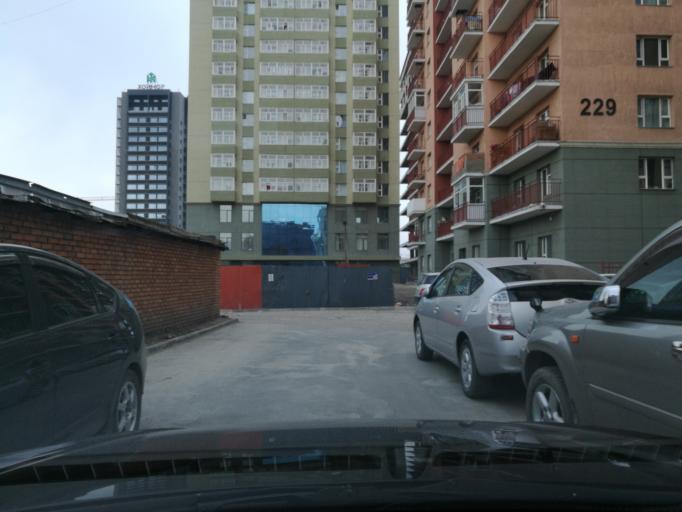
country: MN
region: Ulaanbaatar
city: Ulaanbaatar
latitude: 47.9305
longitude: 106.9143
